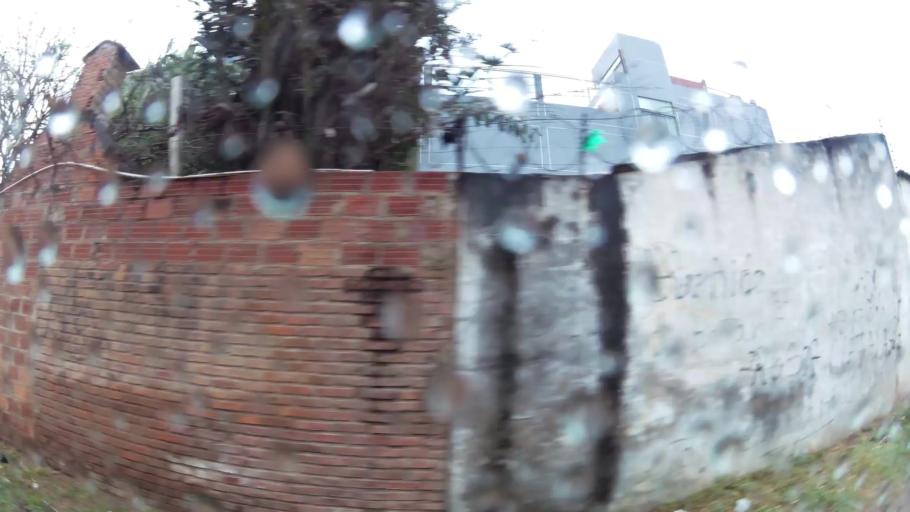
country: BO
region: Santa Cruz
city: Santa Cruz de la Sierra
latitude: -17.7842
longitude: -63.1575
